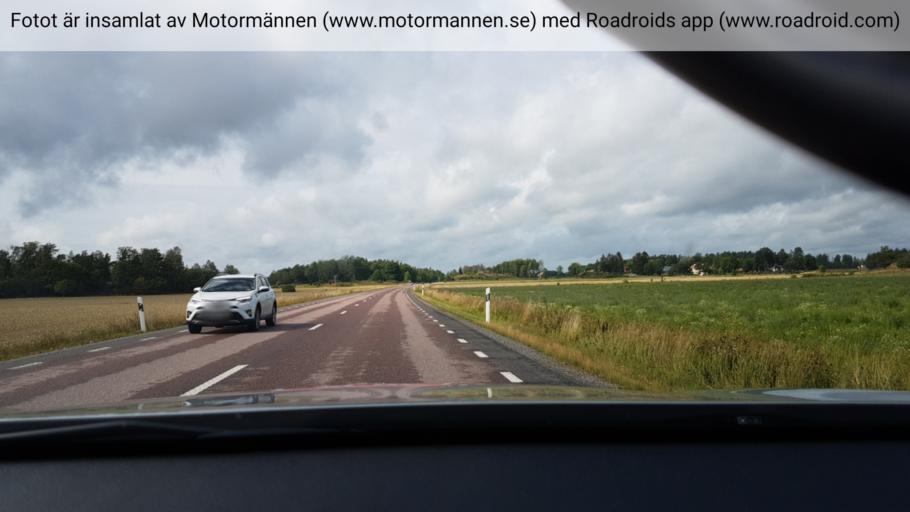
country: SE
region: Uppsala
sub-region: Osthammars Kommun
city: Bjorklinge
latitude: 59.9348
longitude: 17.4675
